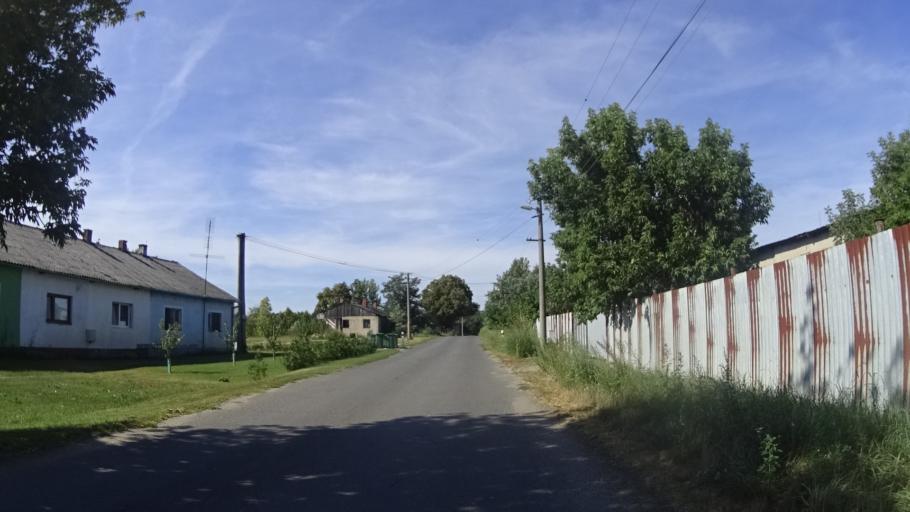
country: AT
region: Lower Austria
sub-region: Politischer Bezirk Ganserndorf
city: Angern an der March
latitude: 48.4121
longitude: 16.8732
